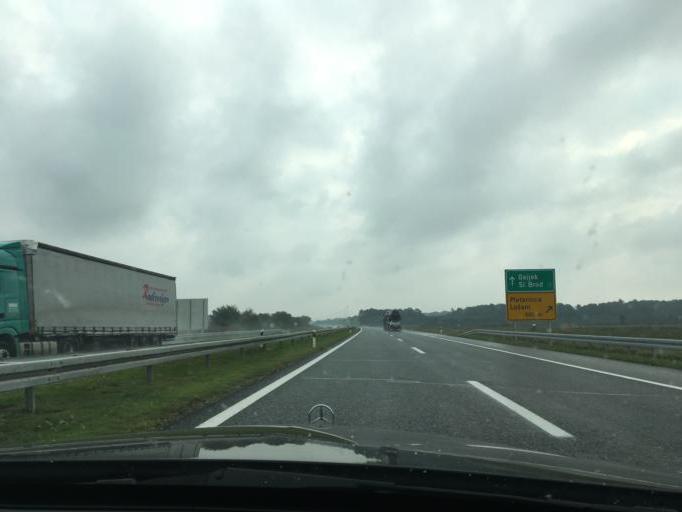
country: HR
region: Brodsko-Posavska
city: Batrina
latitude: 45.1707
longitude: 17.6642
